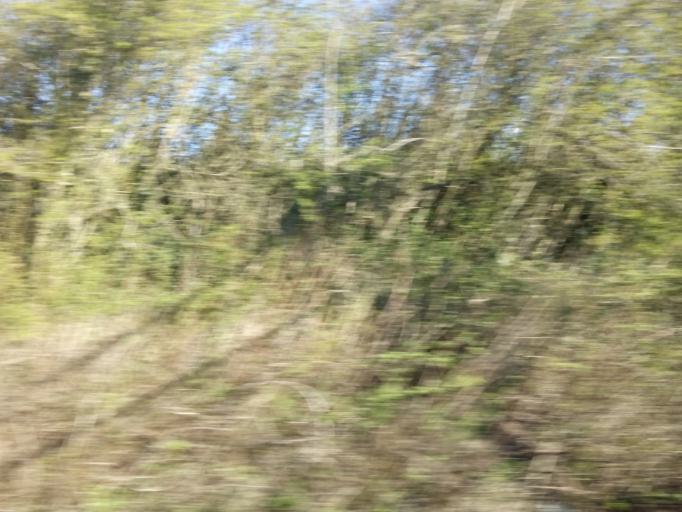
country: GB
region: England
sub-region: Northumberland
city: Pegswood
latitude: 55.1753
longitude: -1.6573
